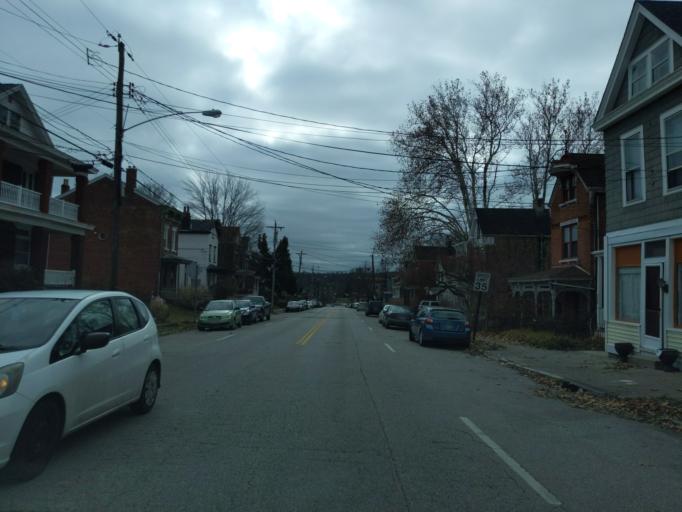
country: US
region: Ohio
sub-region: Hamilton County
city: Finneytown
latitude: 39.1664
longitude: -84.5467
